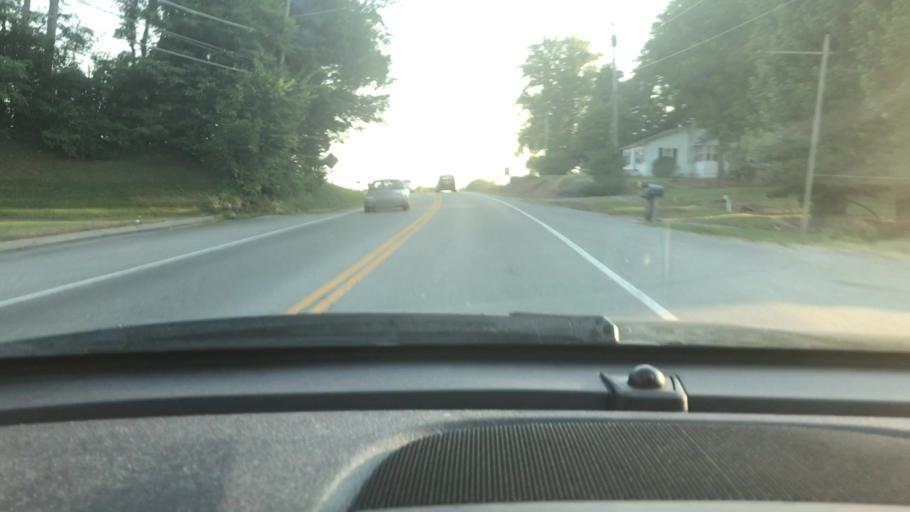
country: US
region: Tennessee
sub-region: Dickson County
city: Charlotte
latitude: 36.1703
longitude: -87.3485
